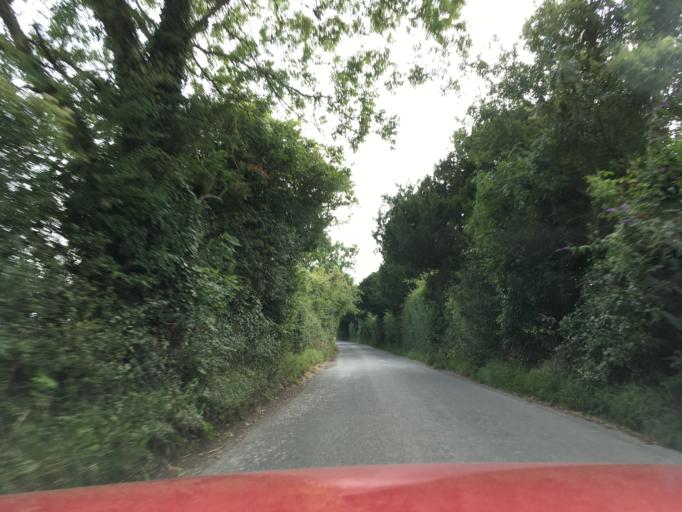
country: GB
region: England
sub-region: Hampshire
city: Colden Common
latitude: 51.0119
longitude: -1.2602
